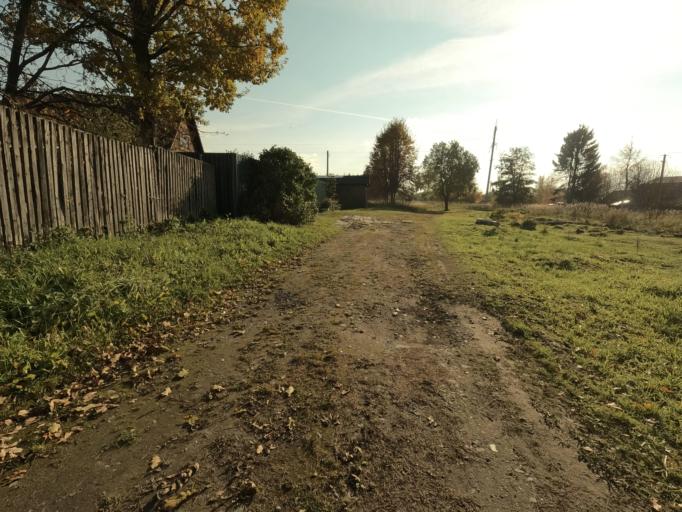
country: RU
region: Leningrad
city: Mga
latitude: 59.7507
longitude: 31.0672
